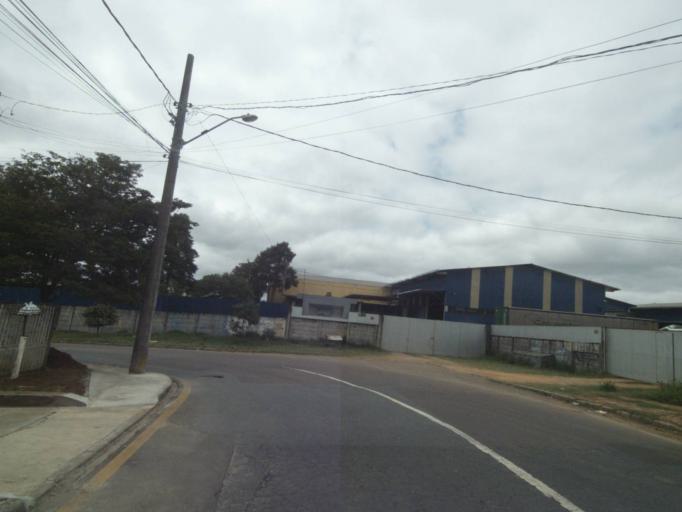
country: BR
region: Parana
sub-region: Sao Jose Dos Pinhais
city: Sao Jose dos Pinhais
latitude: -25.5530
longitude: -49.2737
